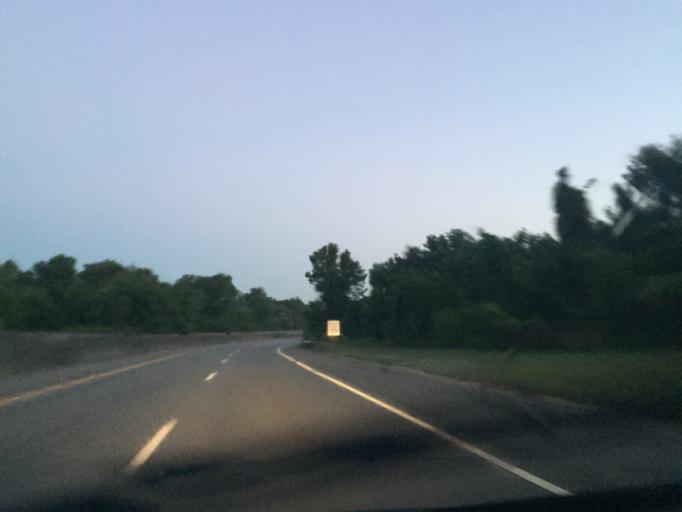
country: US
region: Georgia
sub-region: Chatham County
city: Savannah
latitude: 32.0638
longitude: -81.0740
